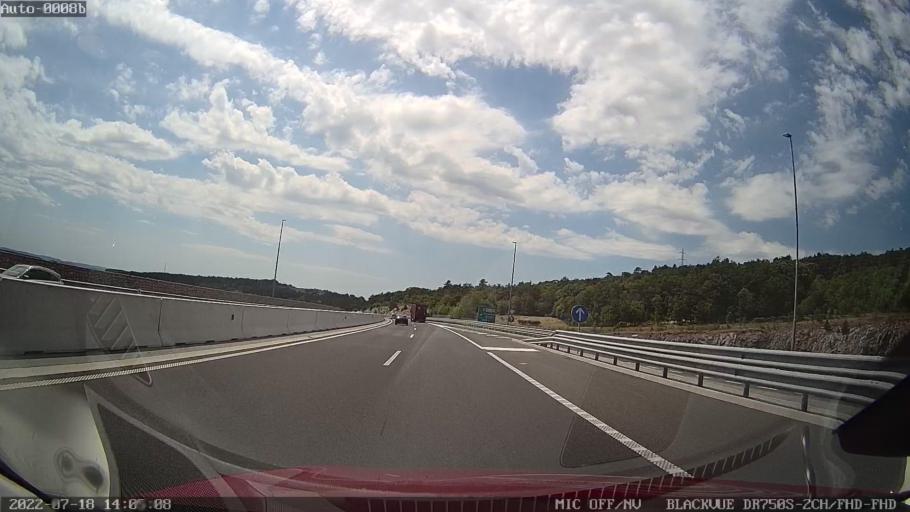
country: SI
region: Hrpelje-Kozina
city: Kozina
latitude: 45.6136
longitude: 13.9367
